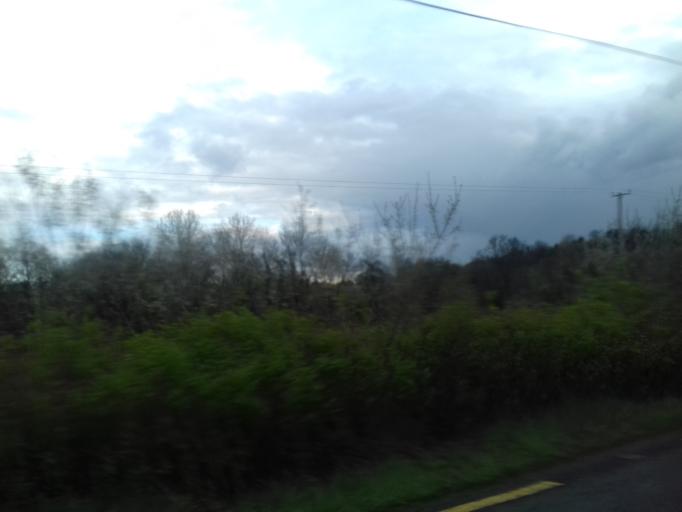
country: IE
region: Ulster
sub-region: An Cabhan
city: Ballyconnell
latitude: 54.0853
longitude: -7.5317
